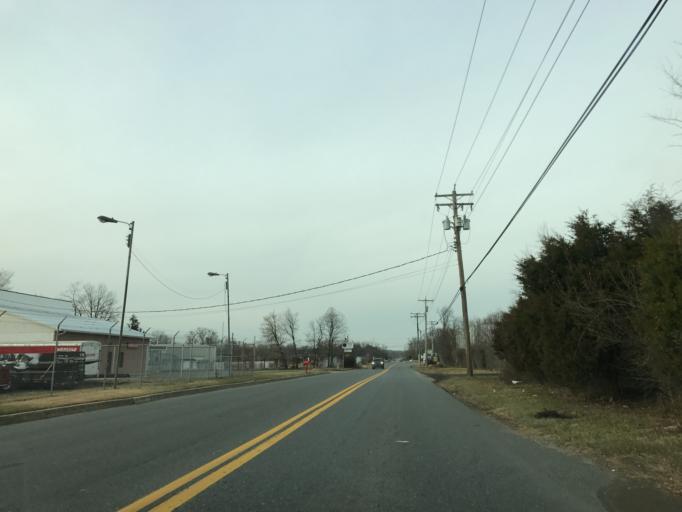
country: US
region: Maryland
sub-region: Baltimore County
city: White Marsh
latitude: 39.3984
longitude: -76.4053
